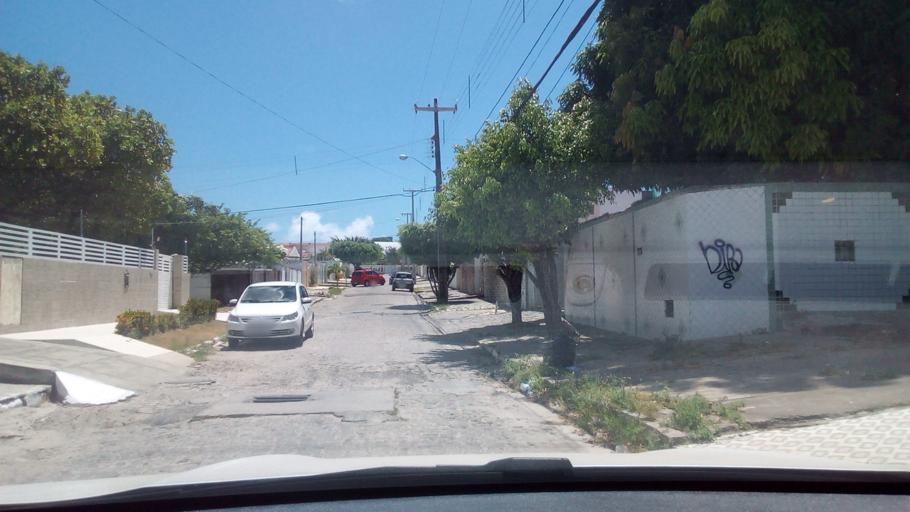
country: BR
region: Paraiba
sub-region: Joao Pessoa
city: Joao Pessoa
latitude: -7.1472
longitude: -34.8394
